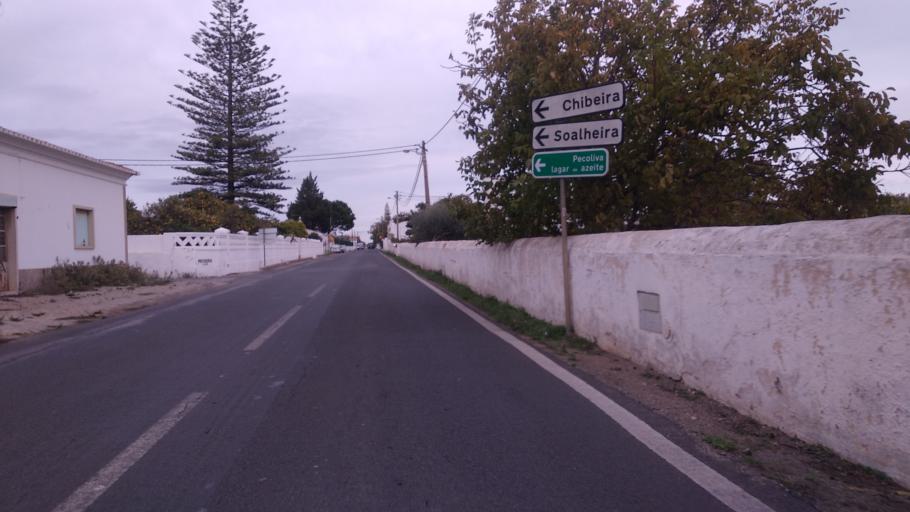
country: PT
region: Faro
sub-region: Sao Bras de Alportel
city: Sao Bras de Alportel
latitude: 37.1524
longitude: -7.9157
